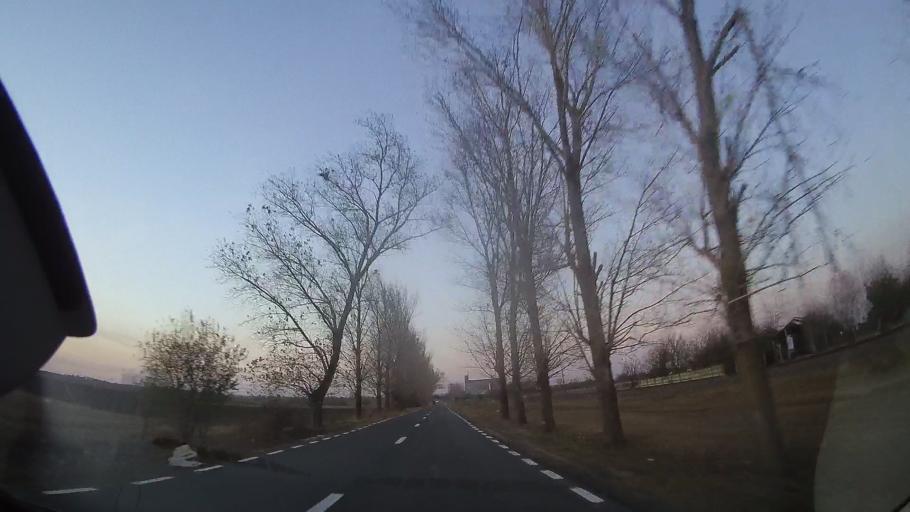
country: RO
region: Constanta
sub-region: Comuna Cobadin
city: Cobadin
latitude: 44.0455
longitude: 28.2530
